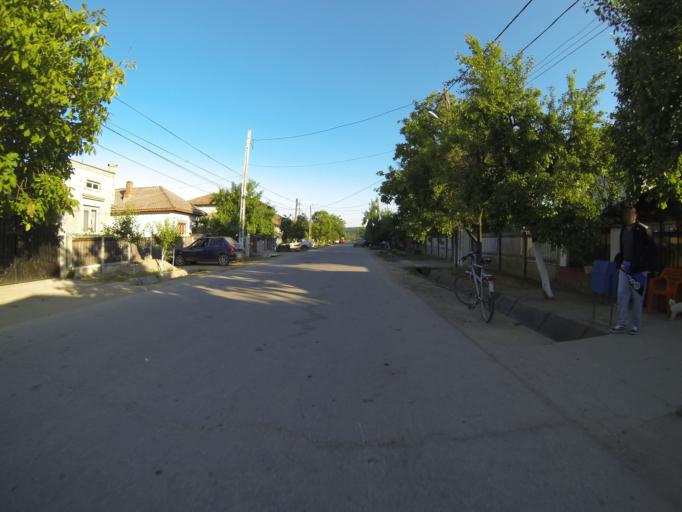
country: RO
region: Dolj
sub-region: Comuna Tuglui
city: Tuglui
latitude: 44.1857
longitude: 23.8131
